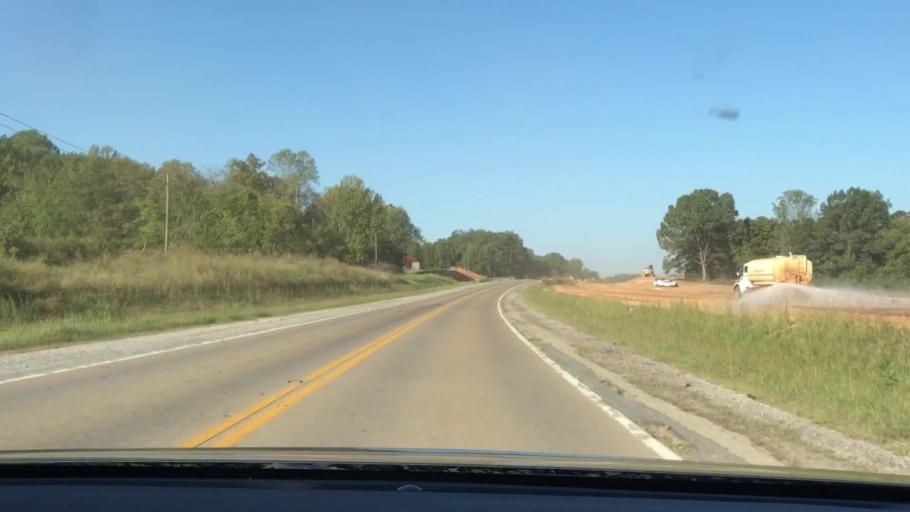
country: US
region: Kentucky
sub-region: Trigg County
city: Cadiz
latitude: 36.7985
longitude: -87.9469
